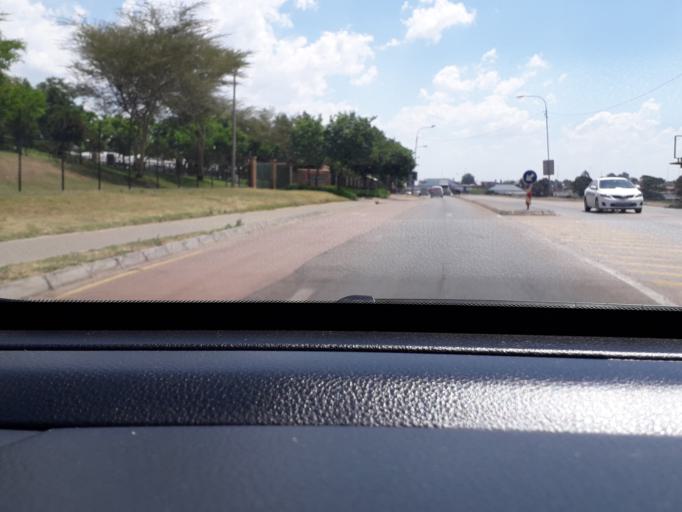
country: ZA
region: Gauteng
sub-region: City of Tshwane Metropolitan Municipality
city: Centurion
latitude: -25.9109
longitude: 28.1690
